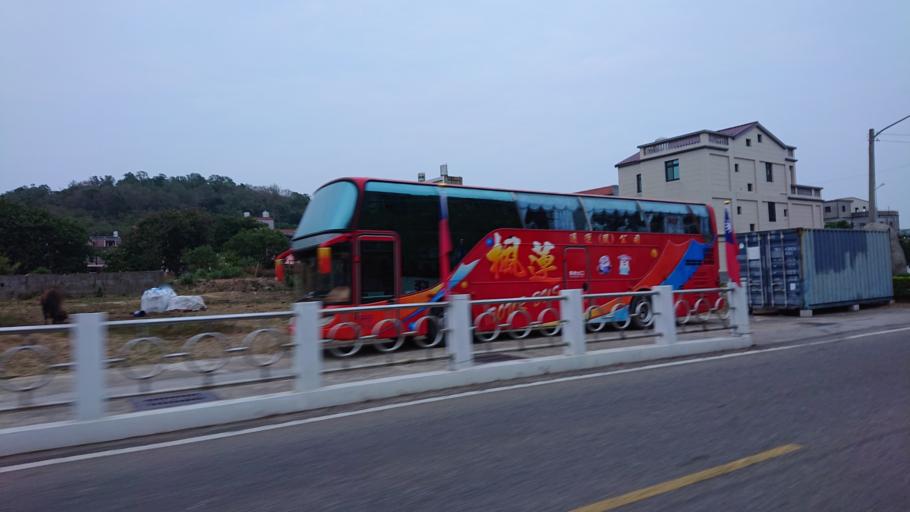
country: TW
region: Fukien
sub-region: Kinmen
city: Jincheng
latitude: 24.4294
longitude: 118.2464
